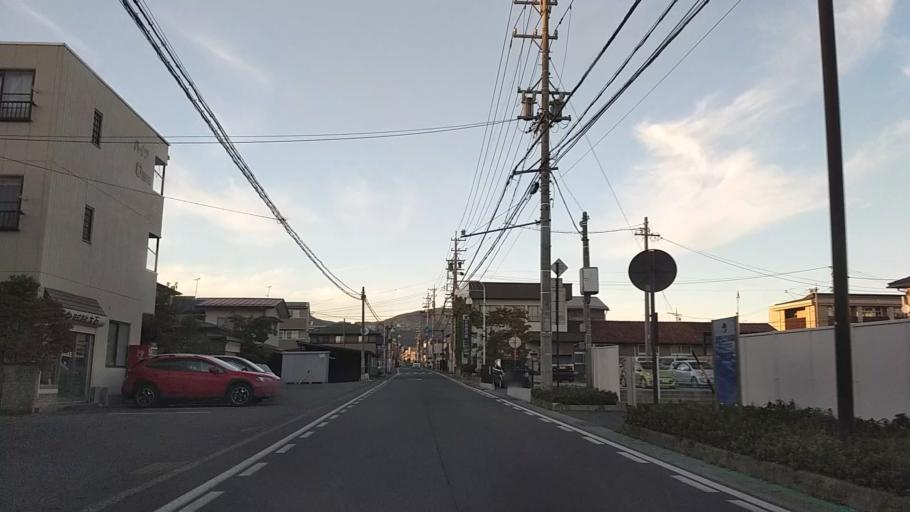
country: JP
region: Nagano
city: Nagano-shi
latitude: 36.6551
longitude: 138.2032
